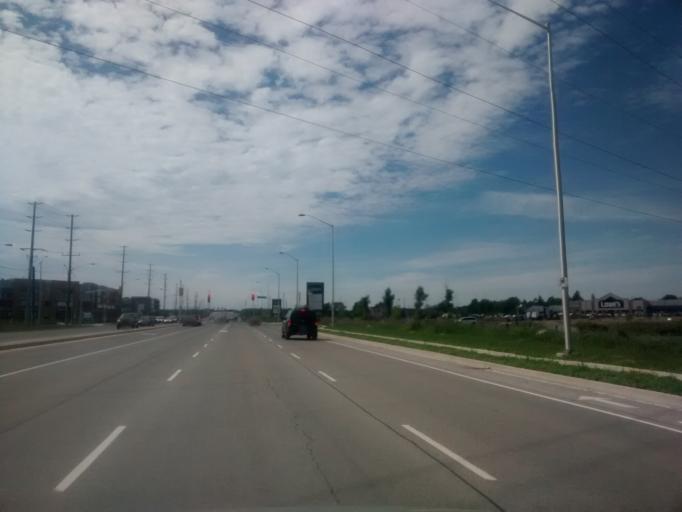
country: CA
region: Ontario
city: Burlington
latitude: 43.4096
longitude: -79.8120
